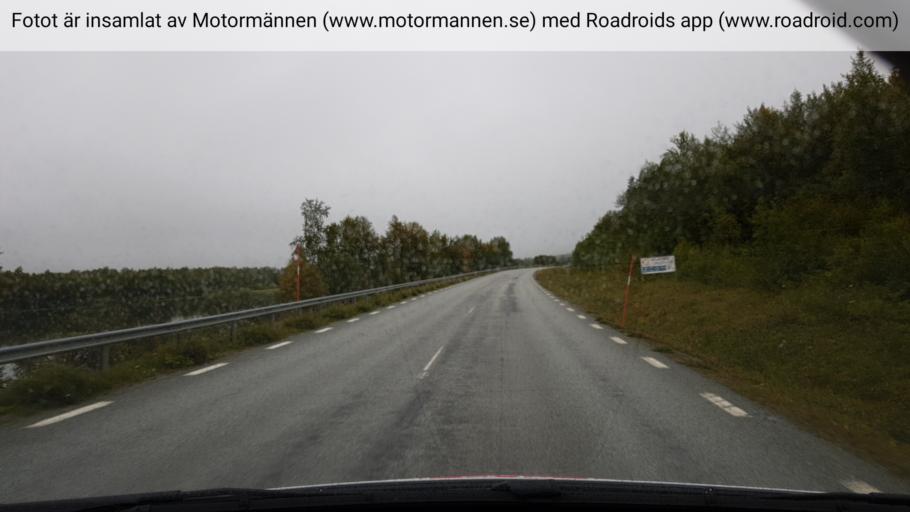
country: NO
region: Nordland
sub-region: Rana
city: Mo i Rana
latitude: 65.7858
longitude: 15.1068
